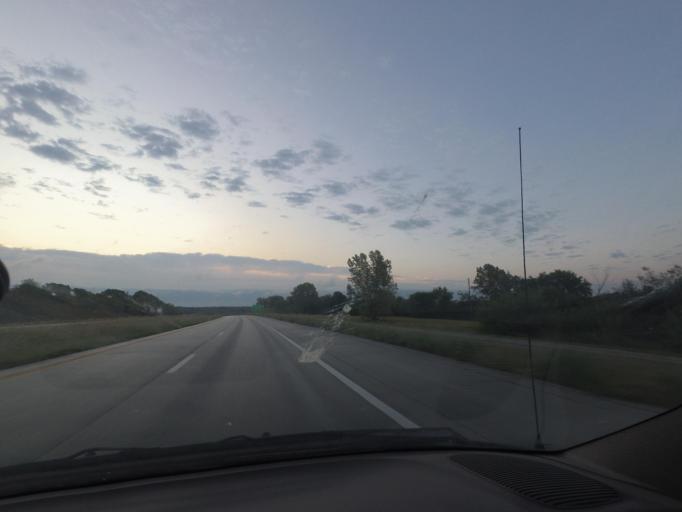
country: US
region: Missouri
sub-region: Macon County
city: Macon
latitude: 39.7504
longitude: -92.5281
